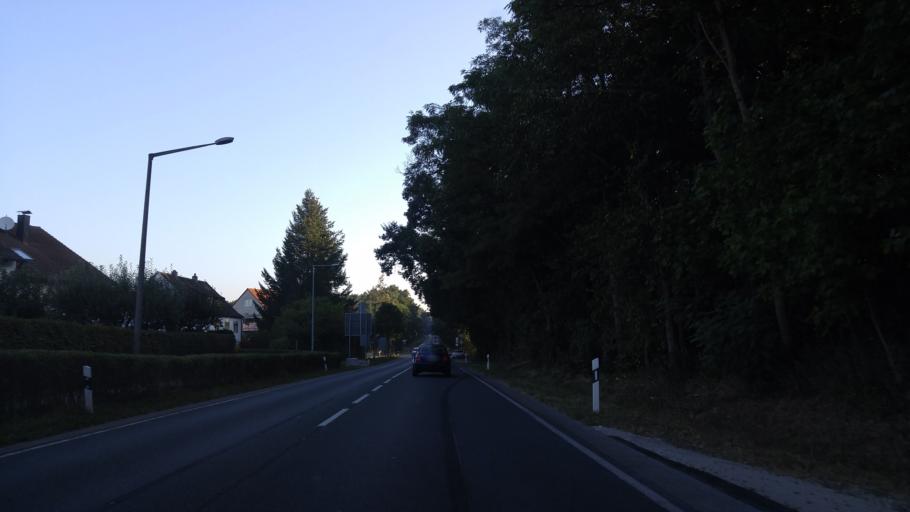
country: DE
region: Bavaria
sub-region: Regierungsbezirk Mittelfranken
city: Furth
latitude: 49.5266
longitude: 10.9784
